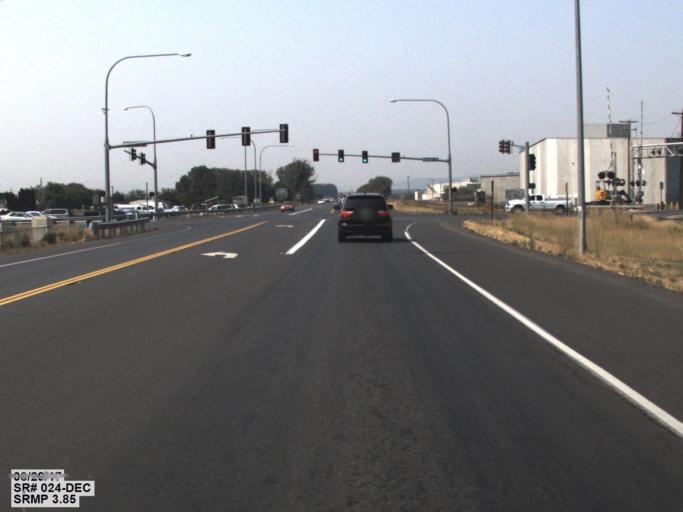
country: US
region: Washington
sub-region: Yakima County
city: Terrace Heights
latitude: 46.5619
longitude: -120.4029
